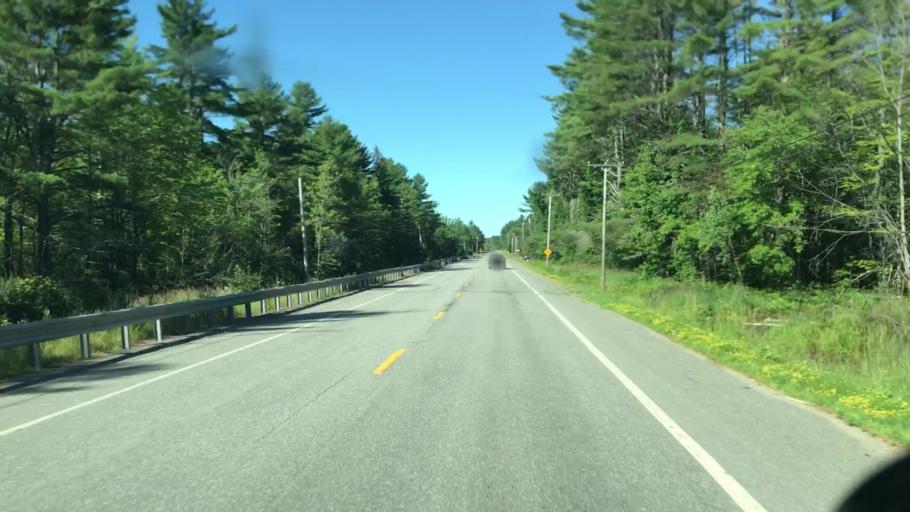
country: US
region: Maine
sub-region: Penobscot County
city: Enfield
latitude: 45.3318
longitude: -68.5845
